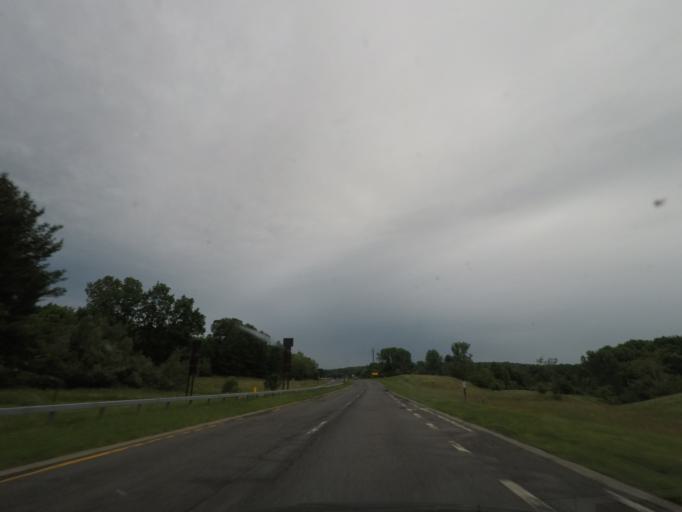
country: US
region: New York
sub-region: Columbia County
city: Chatham
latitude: 42.4132
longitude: -73.5488
